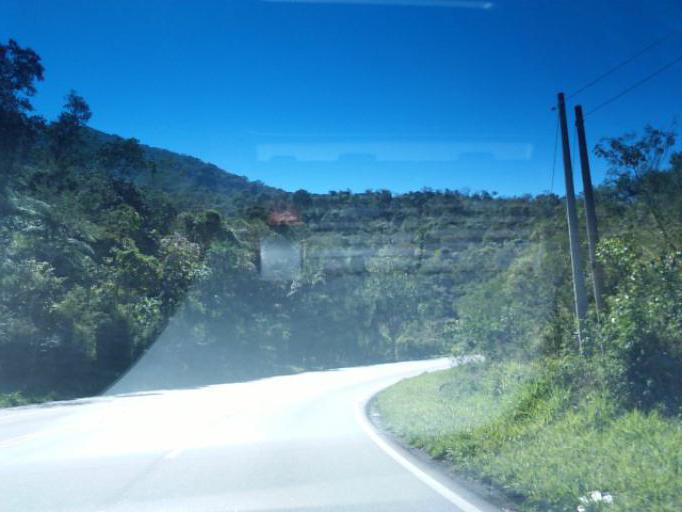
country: BR
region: Sao Paulo
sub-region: Campos Do Jordao
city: Campos do Jordao
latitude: -22.8565
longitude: -45.6219
